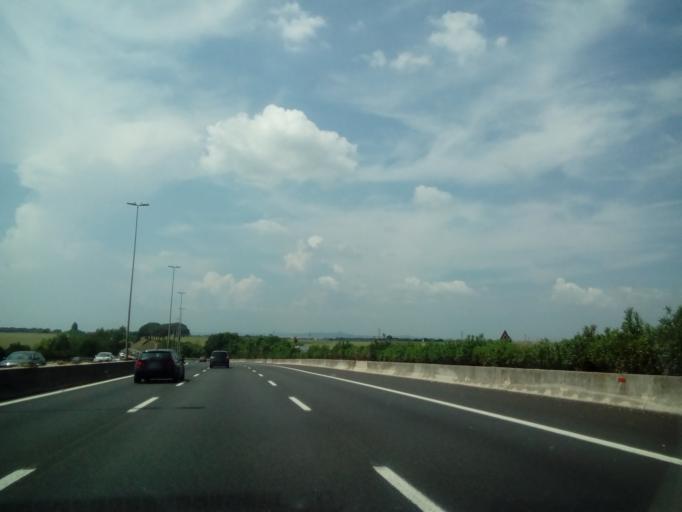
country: IT
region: Latium
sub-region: Citta metropolitana di Roma Capitale
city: Colle Verde
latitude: 41.9584
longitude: 12.5800
